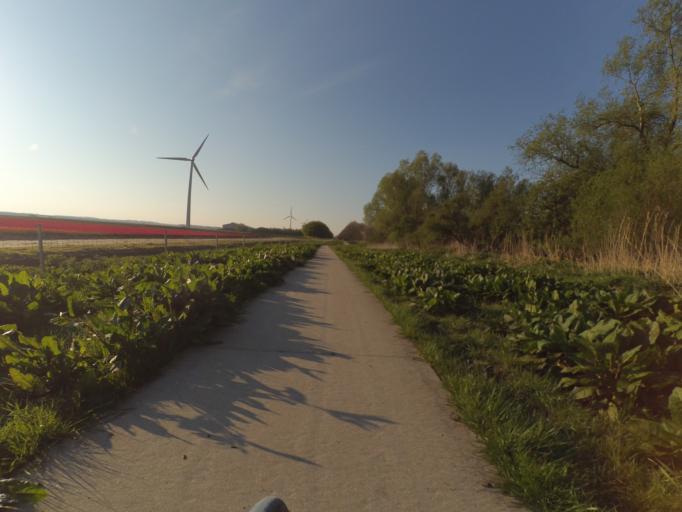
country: NL
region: Flevoland
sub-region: Gemeente Lelystad
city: Lelystad
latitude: 52.4332
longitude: 5.4345
